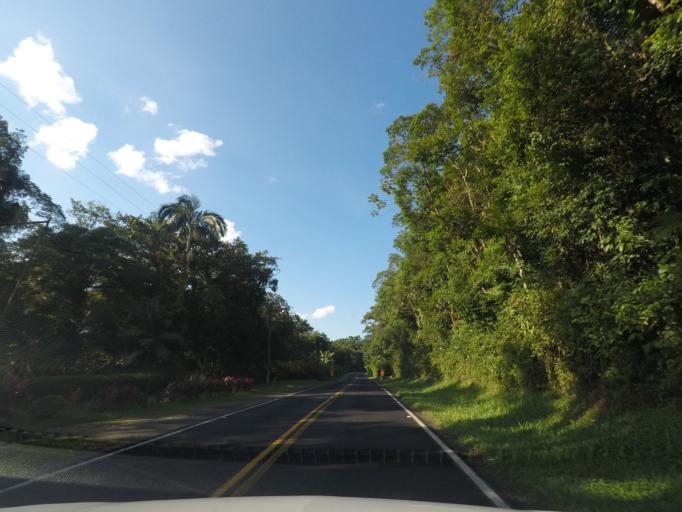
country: BR
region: Parana
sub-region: Antonina
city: Antonina
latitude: -25.3980
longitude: -48.8707
